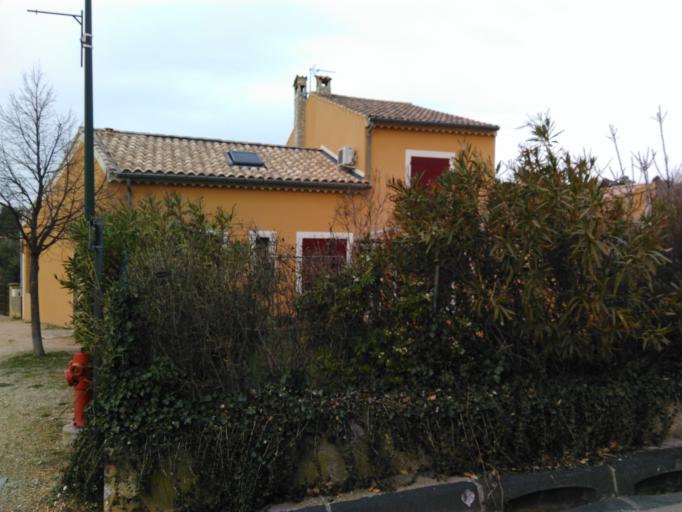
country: FR
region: Provence-Alpes-Cote d'Azur
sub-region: Departement du Vaucluse
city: Villes-sur-Auzon
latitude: 44.1002
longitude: 5.2425
